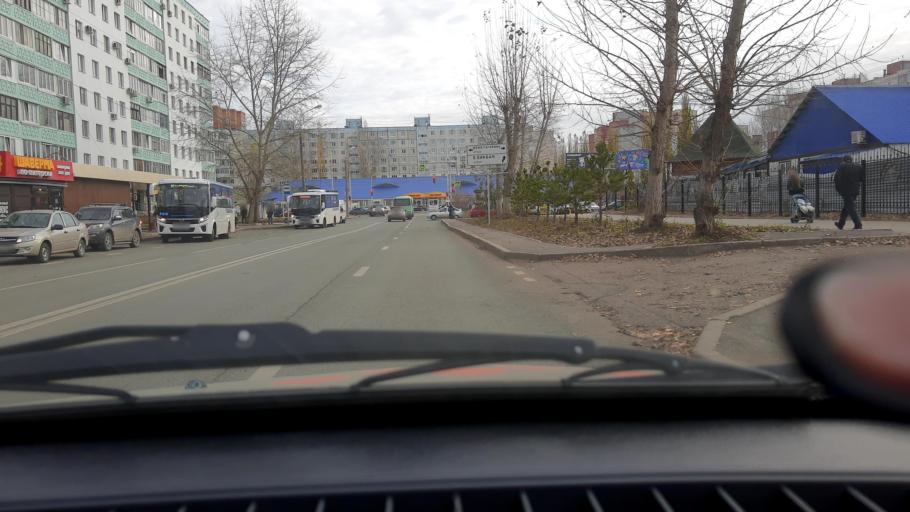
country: RU
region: Bashkortostan
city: Ufa
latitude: 54.7653
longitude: 56.0638
